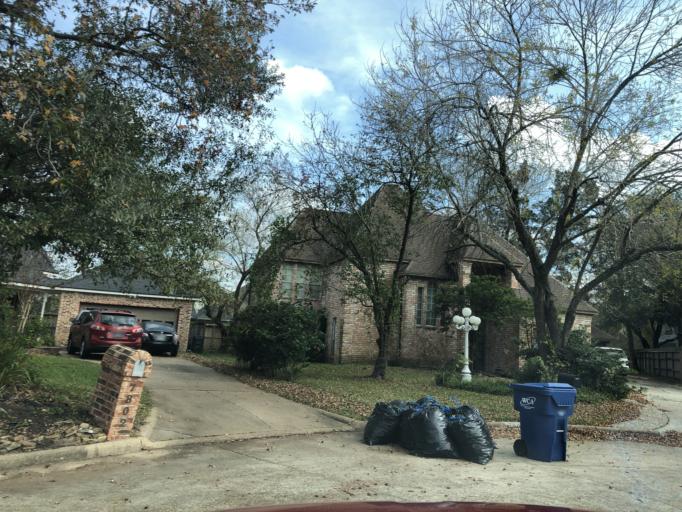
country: US
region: Texas
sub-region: Harris County
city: Tomball
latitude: 30.0333
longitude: -95.5403
